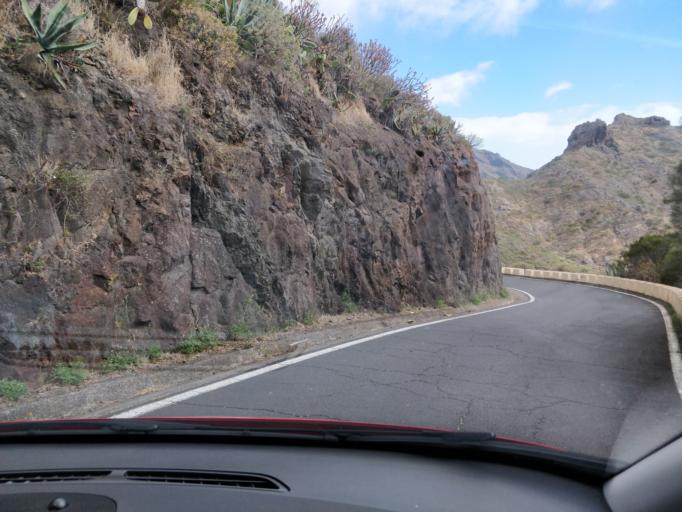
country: ES
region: Canary Islands
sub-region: Provincia de Santa Cruz de Tenerife
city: Santiago del Teide
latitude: 28.3209
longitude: -16.8553
